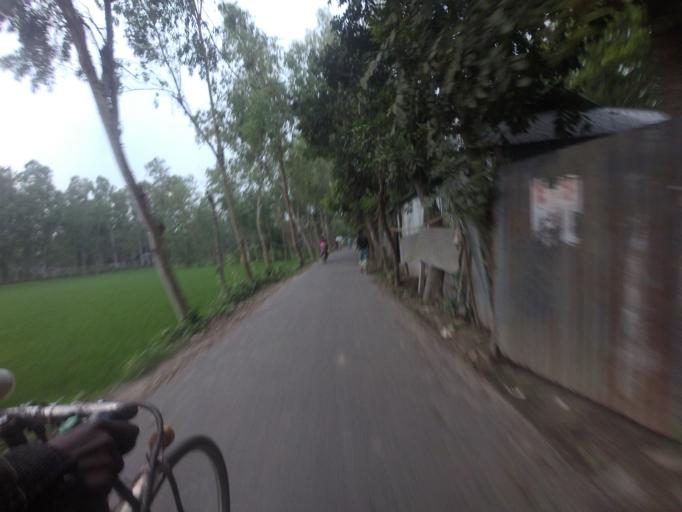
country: BD
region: Rajshahi
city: Sirajganj
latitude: 24.3169
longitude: 89.6582
